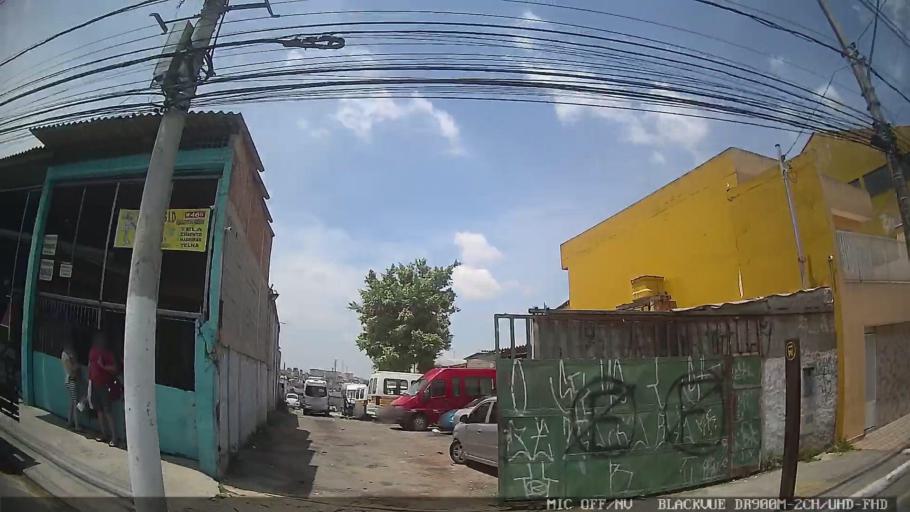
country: BR
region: Sao Paulo
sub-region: Ferraz De Vasconcelos
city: Ferraz de Vasconcelos
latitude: -23.5542
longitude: -46.4025
